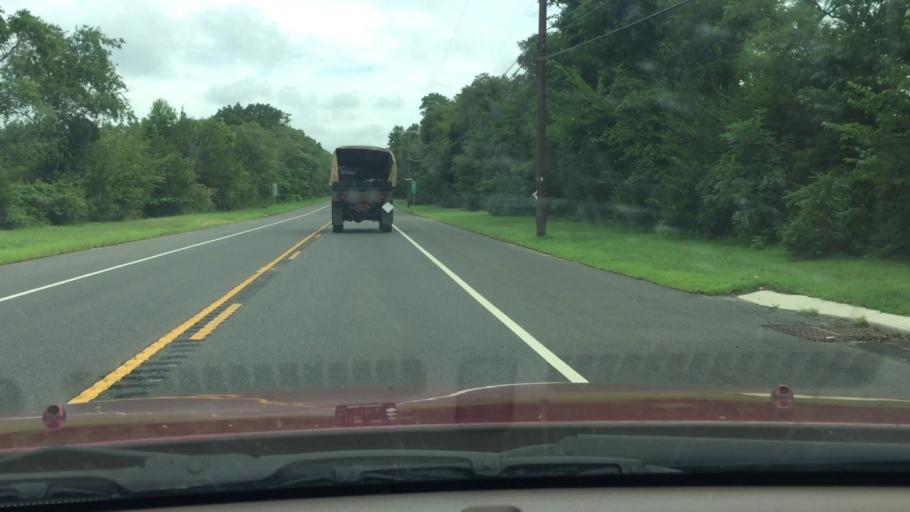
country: US
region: New Jersey
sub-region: Burlington County
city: Fort Dix
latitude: 40.0442
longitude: -74.6458
